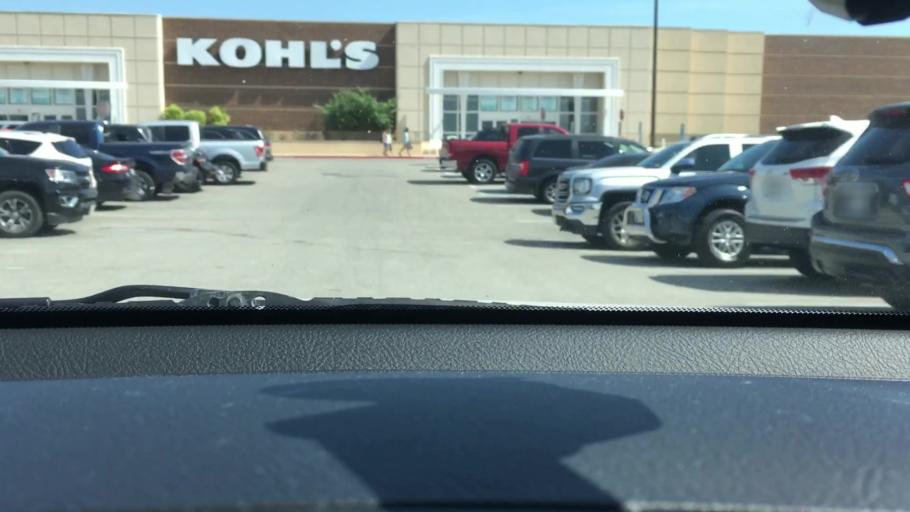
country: US
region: Texas
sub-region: Bexar County
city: Live Oak
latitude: 29.5644
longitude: -98.3271
